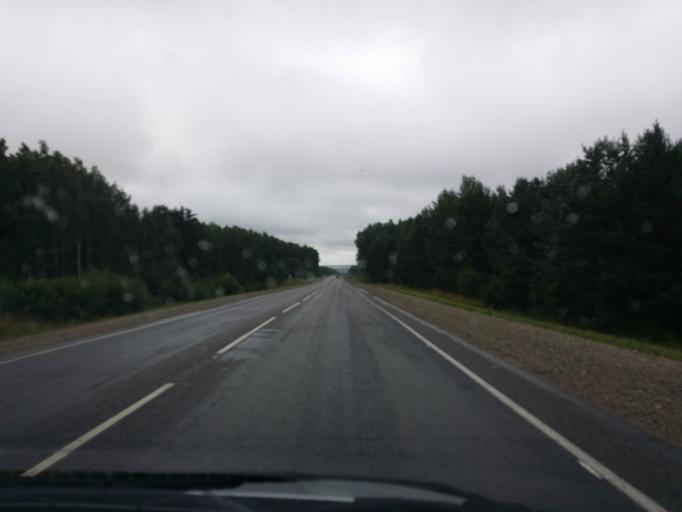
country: RU
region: Altai Krai
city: Troitskoye
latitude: 53.0305
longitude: 84.6976
